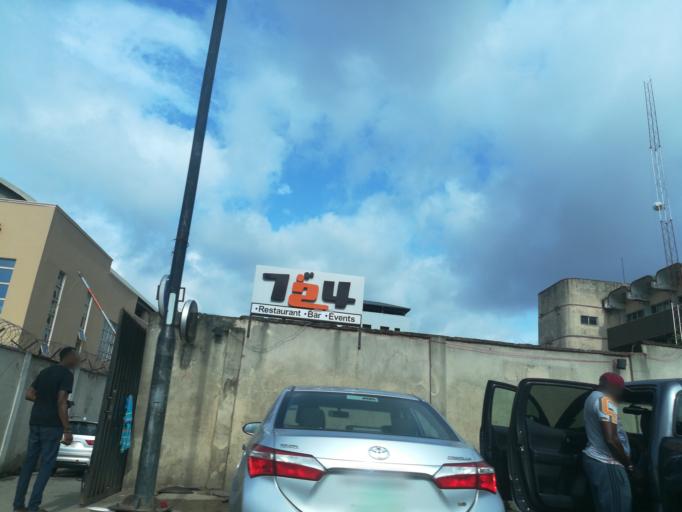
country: NG
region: Lagos
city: Ikeja
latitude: 6.6224
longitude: 3.3564
